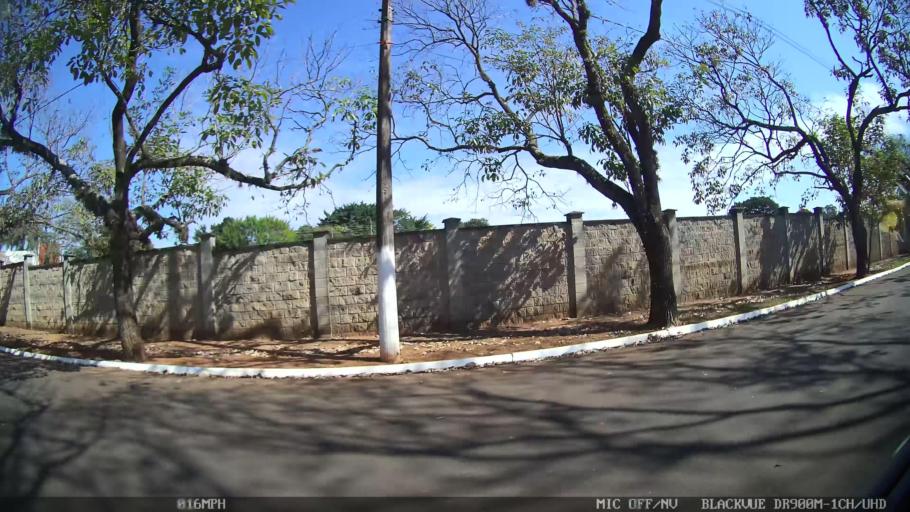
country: BR
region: Sao Paulo
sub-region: Santa Barbara D'Oeste
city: Santa Barbara d'Oeste
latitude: -22.7403
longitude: -47.4132
